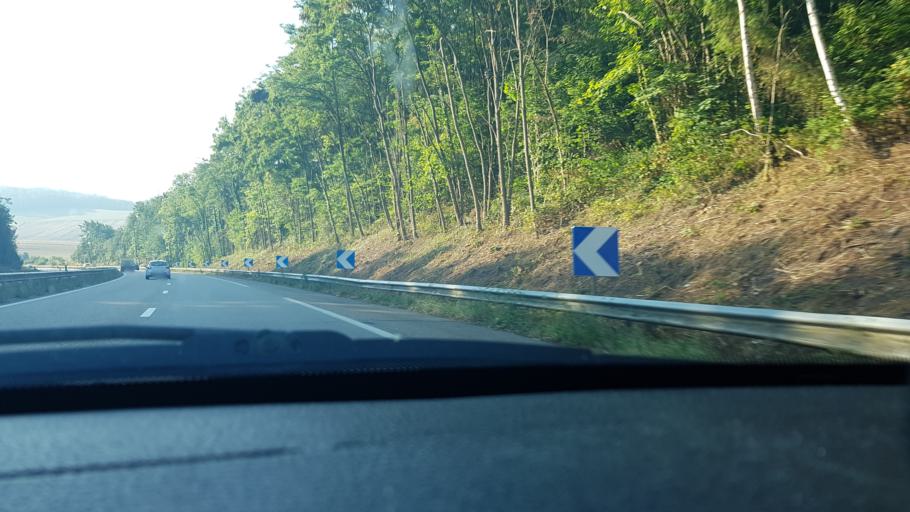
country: FR
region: Lorraine
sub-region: Departement des Vosges
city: Charmes
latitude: 48.3723
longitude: 6.2602
